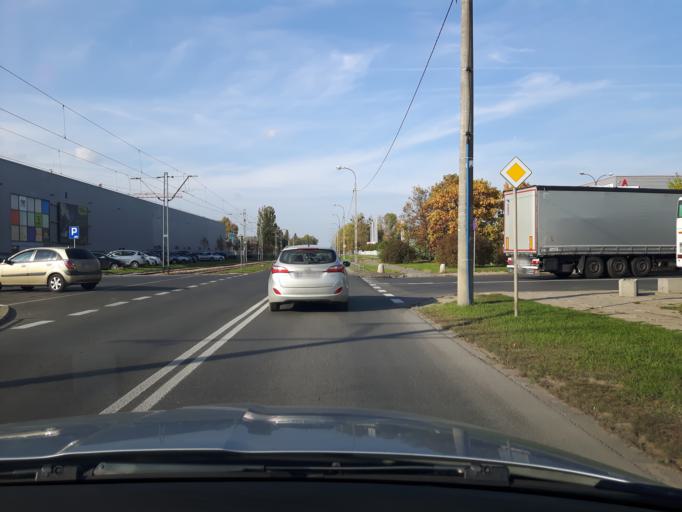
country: PL
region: Masovian Voivodeship
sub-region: Warszawa
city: Targowek
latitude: 52.3019
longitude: 21.0210
